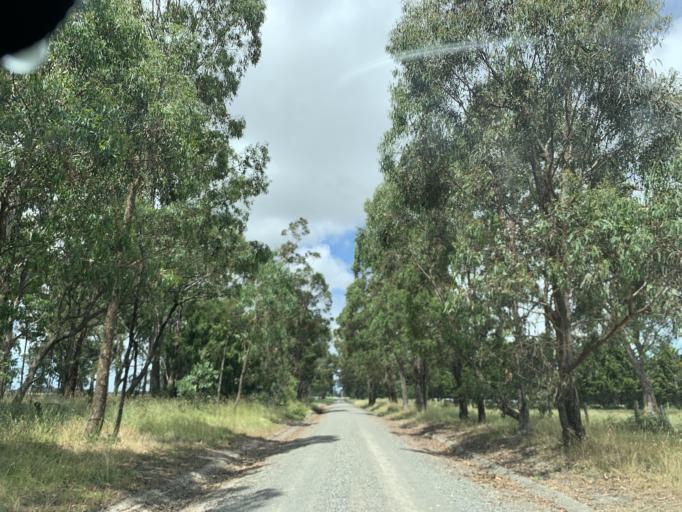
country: AU
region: Victoria
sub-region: Latrobe
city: Traralgon
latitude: -38.1138
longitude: 146.5572
